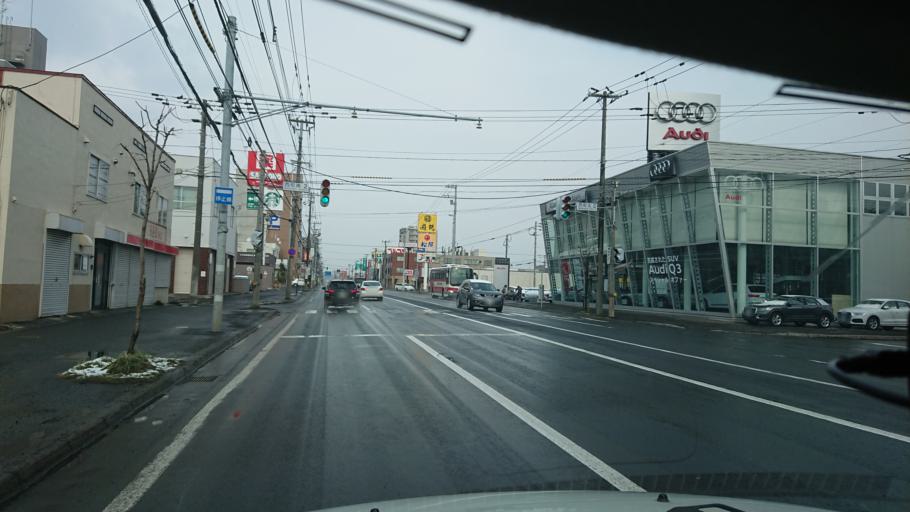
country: JP
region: Hokkaido
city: Sapporo
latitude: 43.0773
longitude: 141.2919
